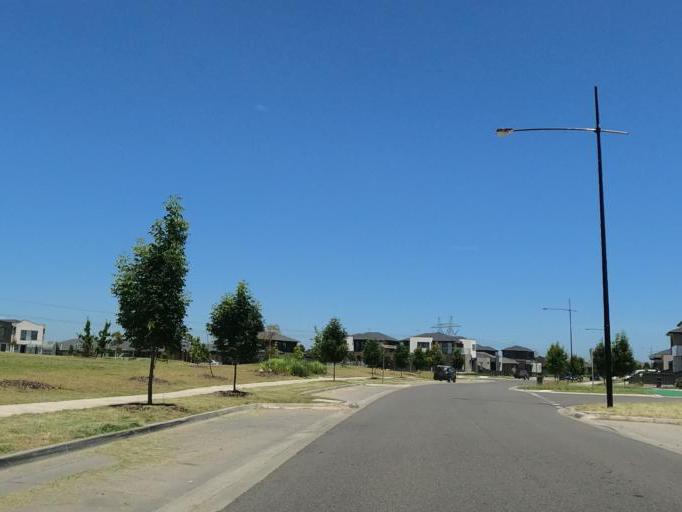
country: AU
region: Victoria
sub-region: Hume
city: Roxburgh Park
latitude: -37.6246
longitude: 144.9170
